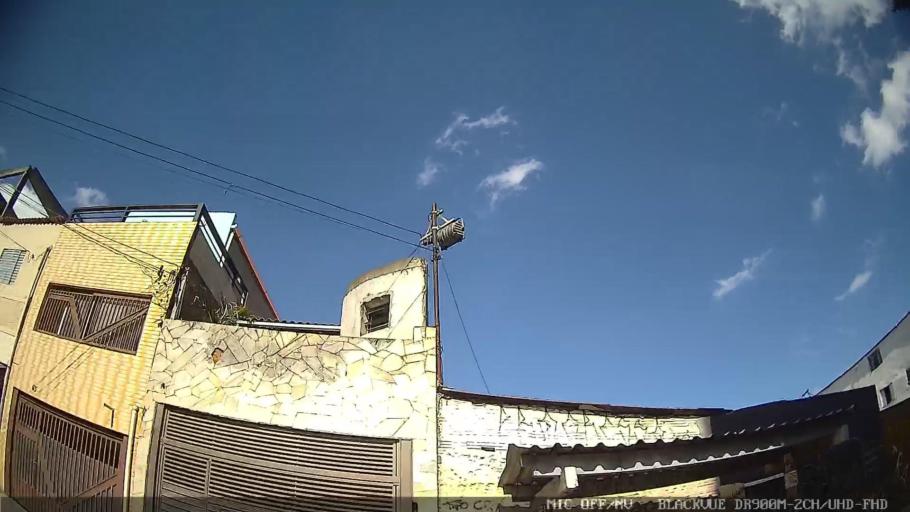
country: BR
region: Sao Paulo
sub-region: Sao Caetano Do Sul
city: Sao Caetano do Sul
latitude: -23.6079
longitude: -46.5980
